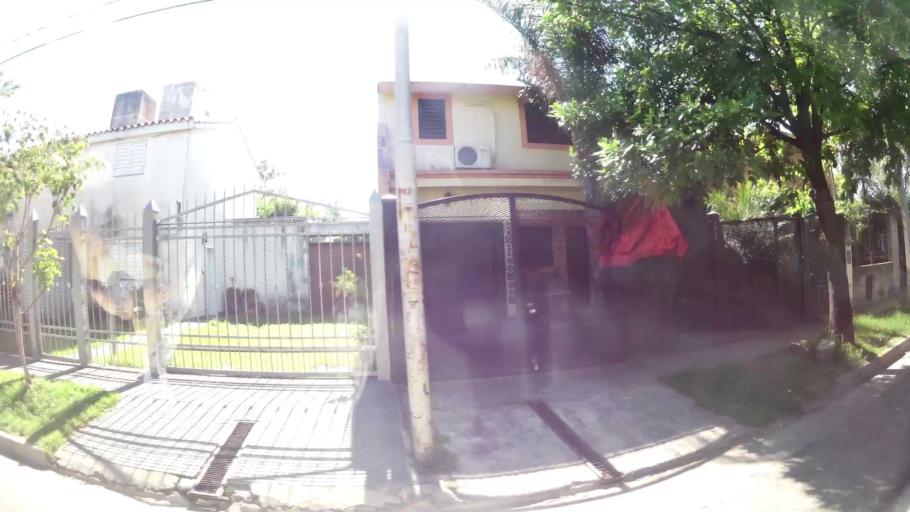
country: AR
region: Cordoba
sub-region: Departamento de Capital
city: Cordoba
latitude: -31.3576
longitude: -64.1847
